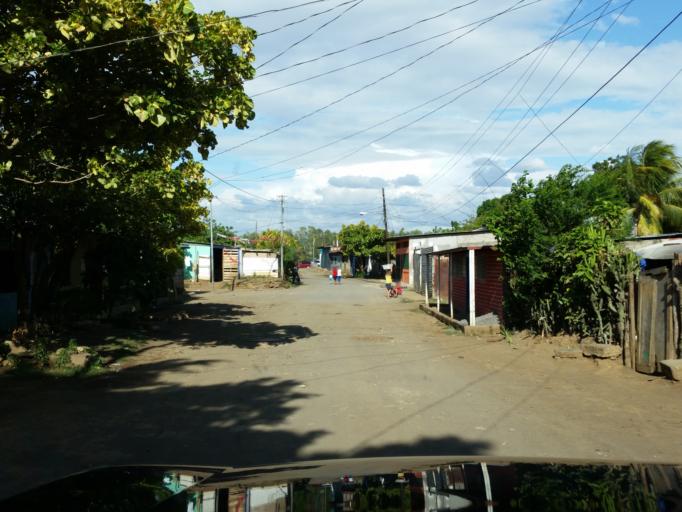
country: NI
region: Managua
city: Managua
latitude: 12.1322
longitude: -86.2764
